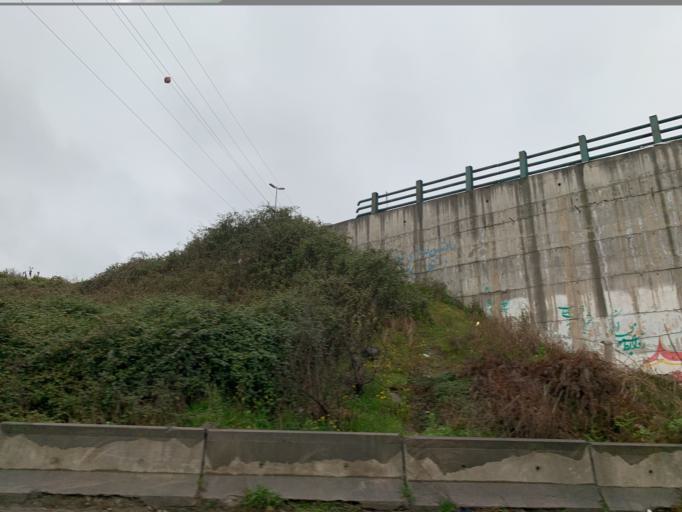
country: IR
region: Mazandaran
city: Amol
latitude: 36.3993
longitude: 52.3467
